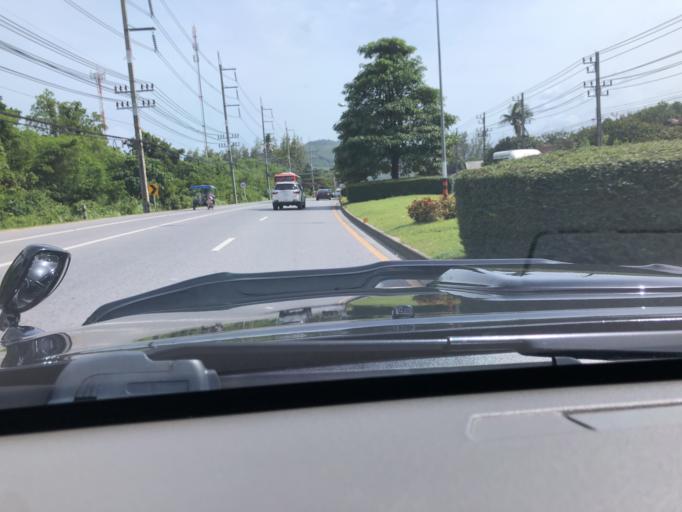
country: TH
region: Phuket
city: Thalang
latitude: 8.1019
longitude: 98.3347
